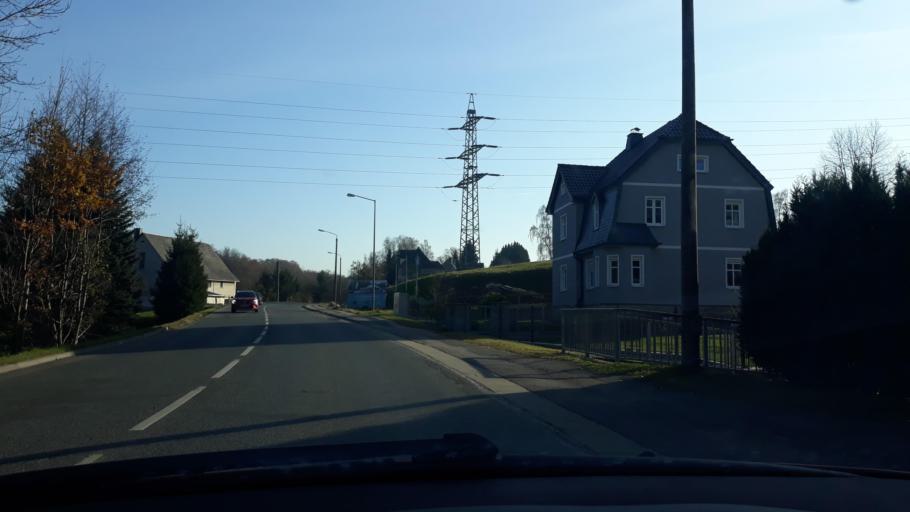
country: DE
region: Saxony
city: Kirchberg
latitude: 50.6360
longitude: 12.5184
